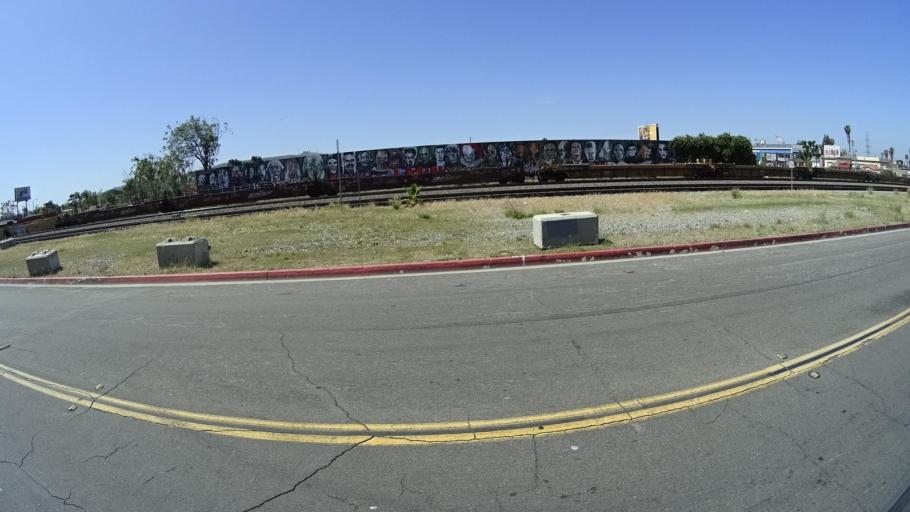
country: US
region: California
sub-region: Los Angeles County
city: Avocado Heights
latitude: 34.0517
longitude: -117.9979
